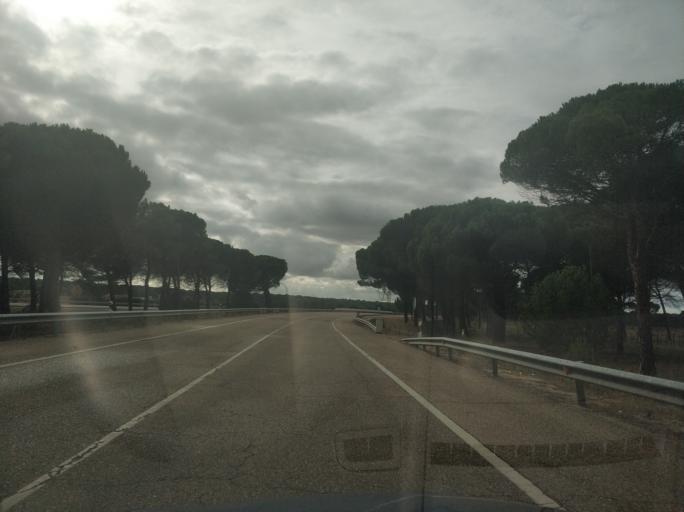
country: ES
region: Castille and Leon
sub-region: Provincia de Valladolid
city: Torrecilla de la Abadesa
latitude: 41.4798
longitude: -5.0474
